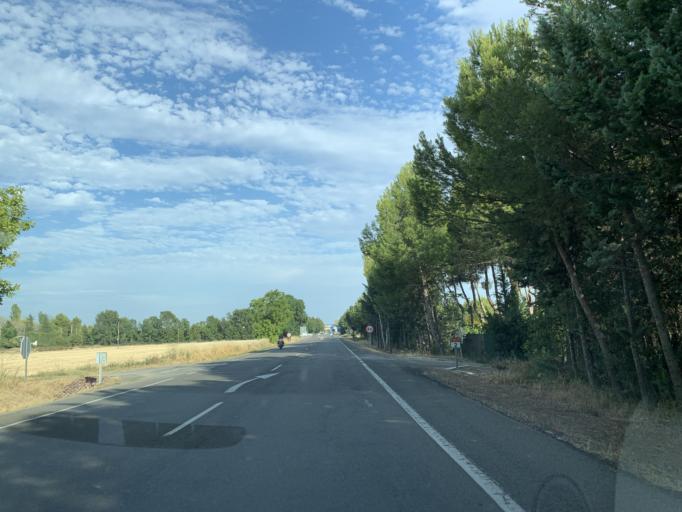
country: ES
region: Aragon
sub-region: Provincia de Huesca
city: Chimillas
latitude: 42.1519
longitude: -0.4335
